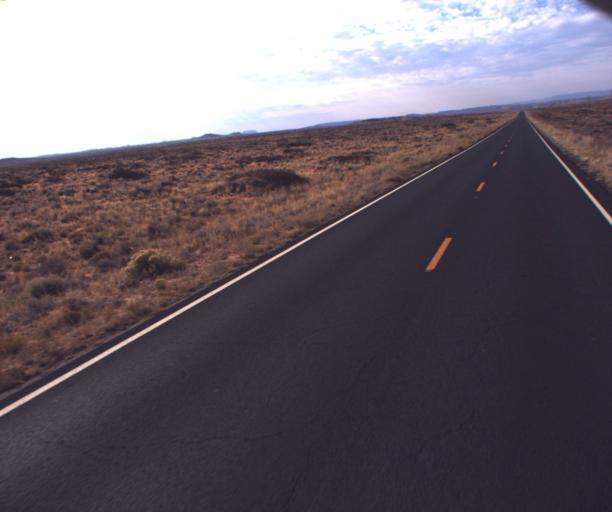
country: US
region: Arizona
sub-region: Apache County
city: Many Farms
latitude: 36.8539
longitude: -109.6375
